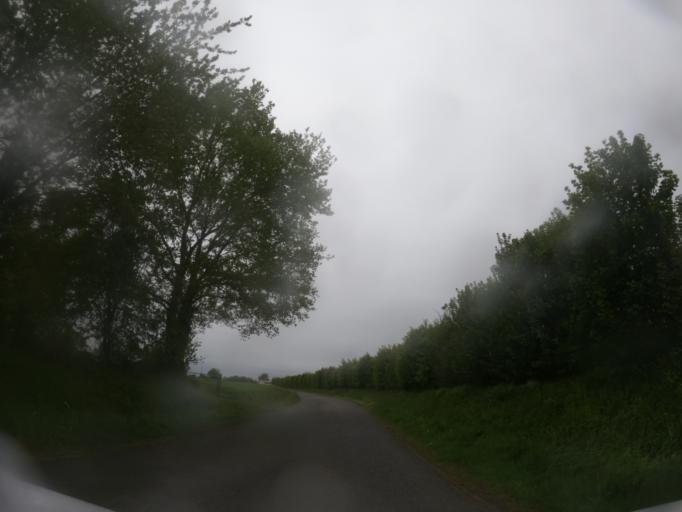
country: FR
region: Brittany
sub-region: Departement d'Ille-et-Vilaine
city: La Guerche-de-Bretagne
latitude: 47.9498
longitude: -1.1338
